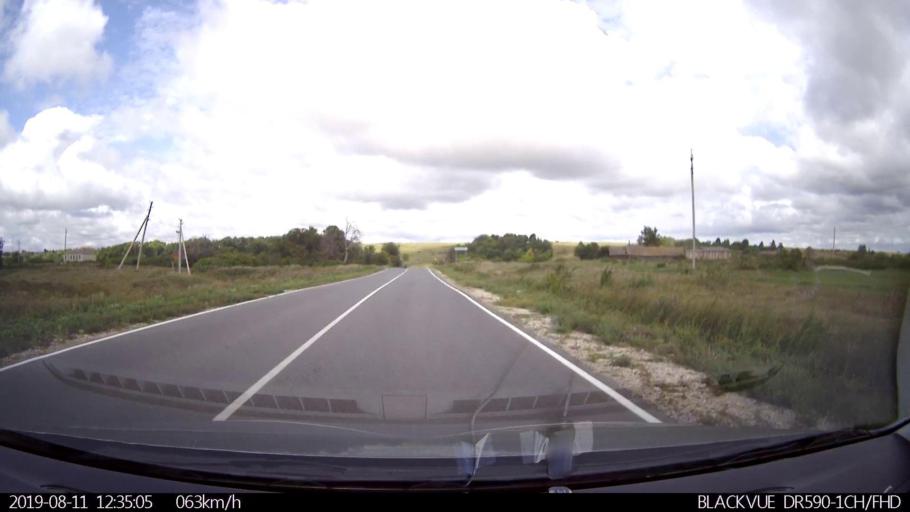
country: RU
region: Ulyanovsk
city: Ignatovka
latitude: 53.8214
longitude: 47.8352
